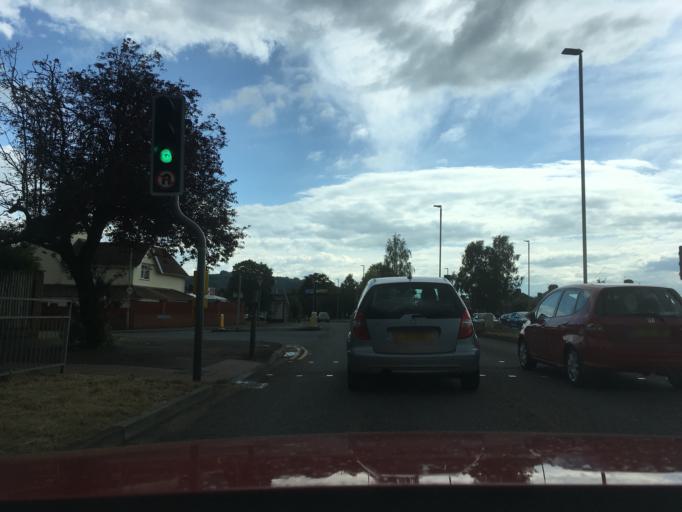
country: GB
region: England
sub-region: Gloucestershire
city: Gloucester
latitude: 51.8545
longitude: -2.2238
